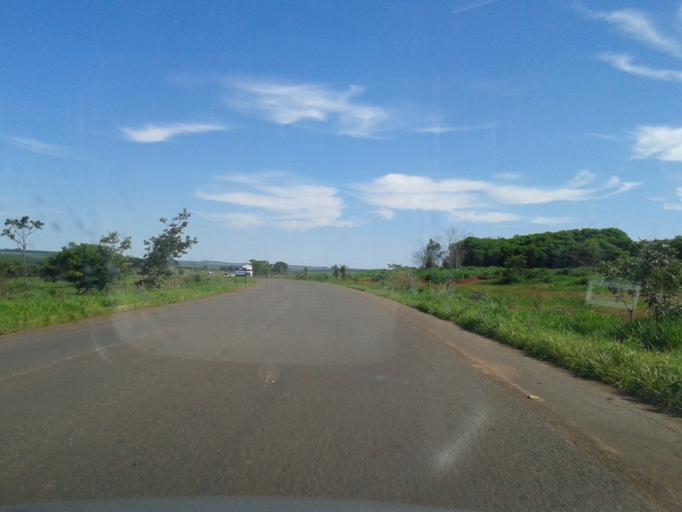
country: BR
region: Goias
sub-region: Bela Vista De Goias
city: Bela Vista de Goias
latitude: -17.1827
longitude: -48.7162
